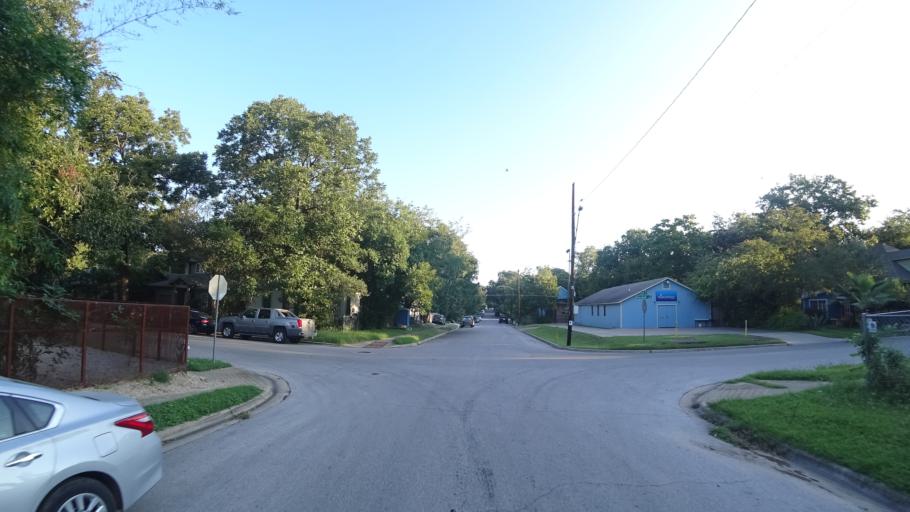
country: US
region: Texas
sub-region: Travis County
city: Austin
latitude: 30.2520
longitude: -97.7255
